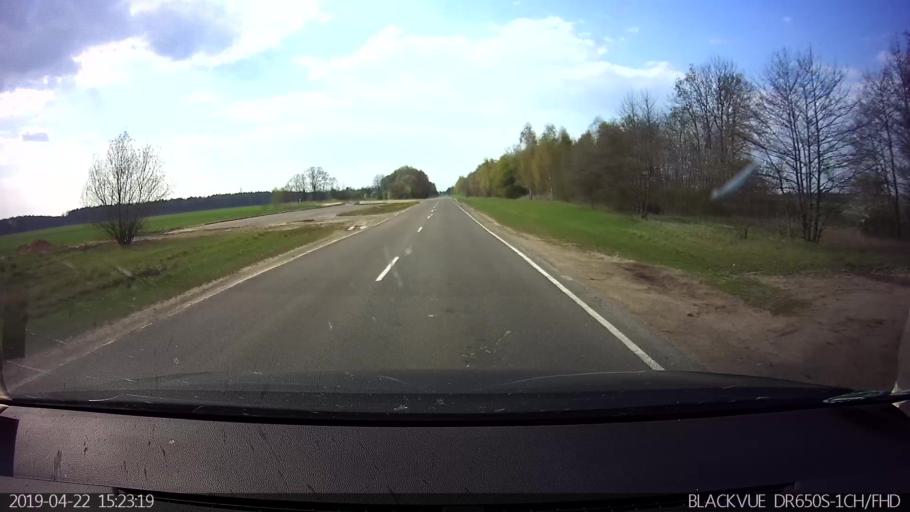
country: BY
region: Brest
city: Vysokaye
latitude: 52.3544
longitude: 23.4290
